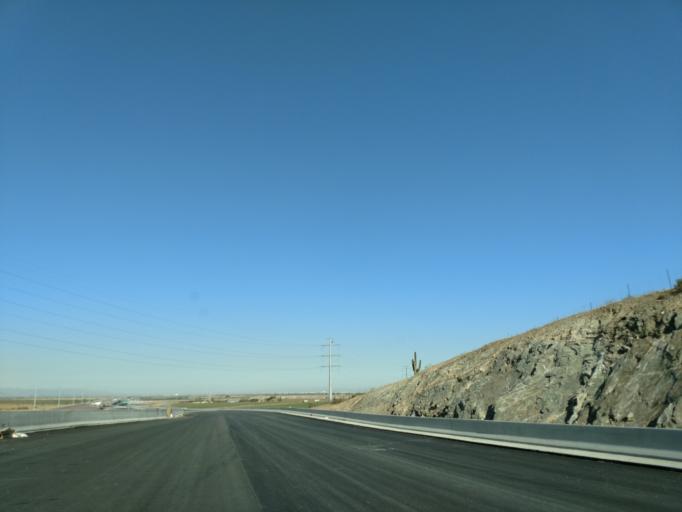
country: US
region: Arizona
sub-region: Maricopa County
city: Laveen
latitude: 33.3222
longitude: -112.1641
